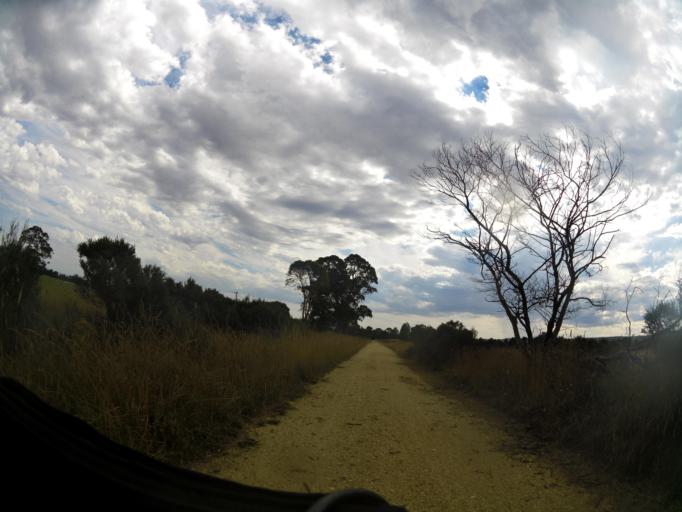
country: AU
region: Victoria
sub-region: Wellington
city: Heyfield
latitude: -38.0471
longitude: 146.6361
